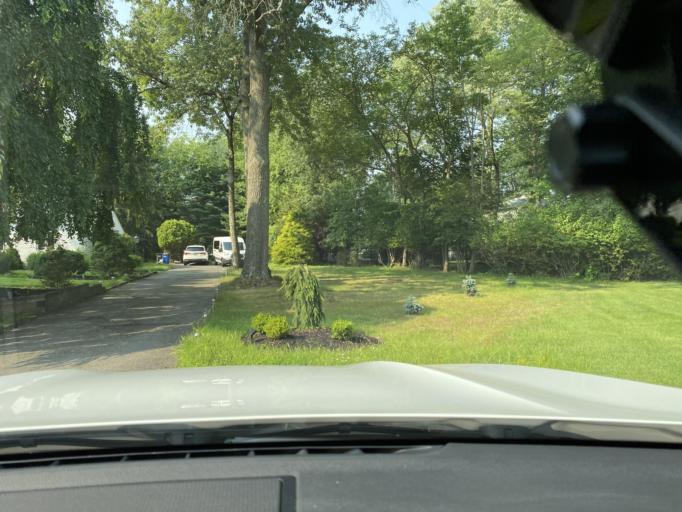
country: US
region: New York
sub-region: Rockland County
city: Airmont
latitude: 41.0847
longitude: -74.1129
